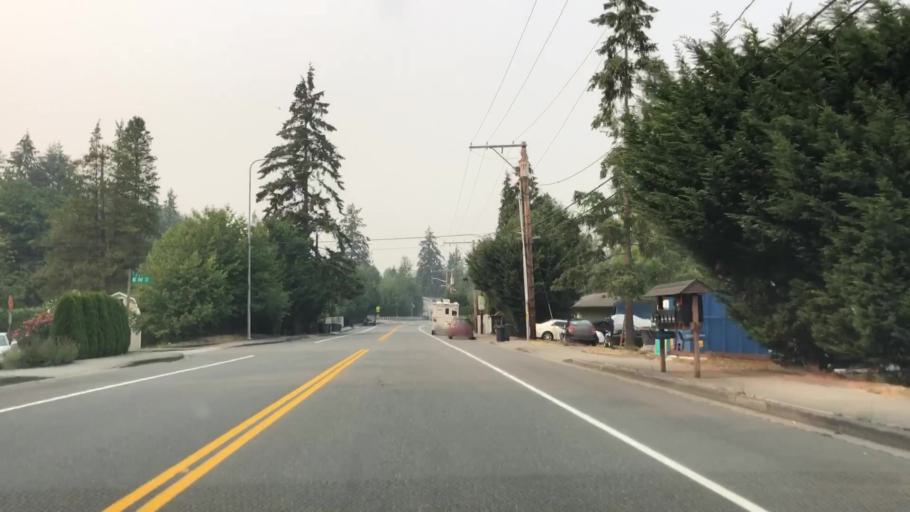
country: US
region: Washington
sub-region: King County
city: Kenmore
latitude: 47.7658
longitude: -122.2426
